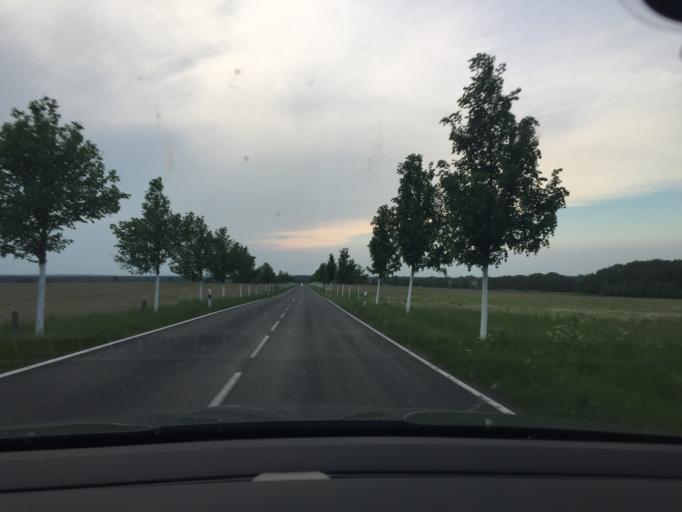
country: DE
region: Brandenburg
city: Niemegk
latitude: 52.0518
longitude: 12.7005
